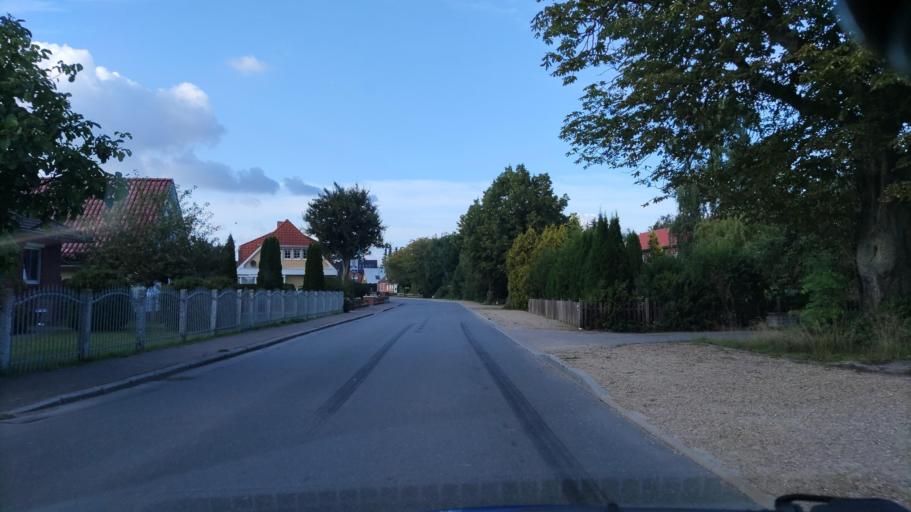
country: DE
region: Schleswig-Holstein
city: Glasau
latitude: 54.0544
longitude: 10.5312
